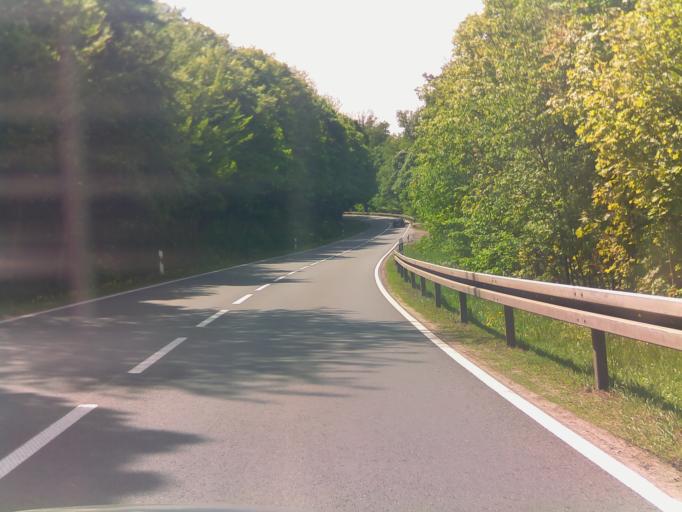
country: DE
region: Saxony-Anhalt
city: Huttenrode
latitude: 51.7280
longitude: 10.8985
